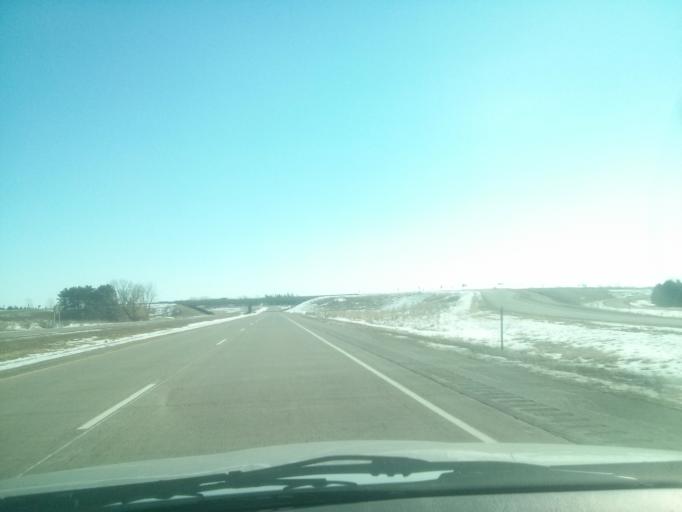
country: US
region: Wisconsin
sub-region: Saint Croix County
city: New Richmond
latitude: 45.1225
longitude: -92.5943
